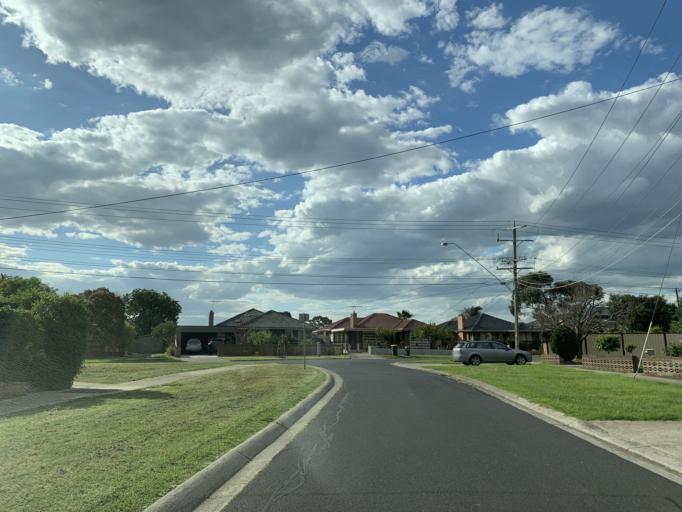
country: AU
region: Victoria
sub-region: Moonee Valley
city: Essendon West
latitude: -37.7539
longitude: 144.8585
